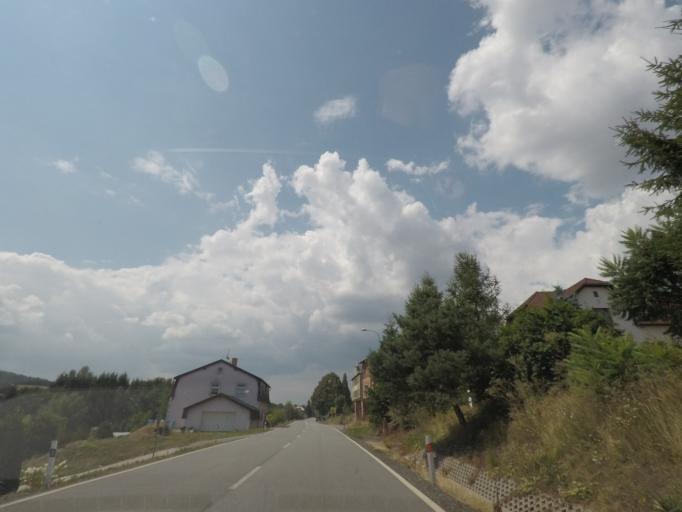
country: CZ
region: Kralovehradecky
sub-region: Okres Jicin
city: Pecka
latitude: 50.5315
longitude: 15.6094
